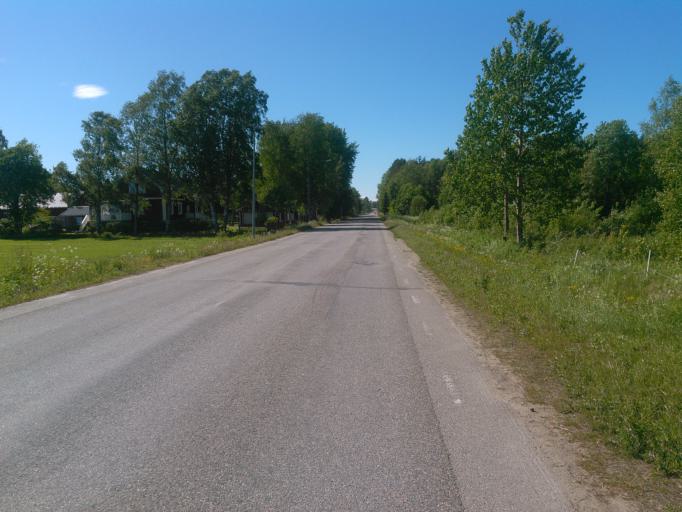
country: SE
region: Vaesterbotten
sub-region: Umea Kommun
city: Roback
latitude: 63.8212
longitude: 20.1923
